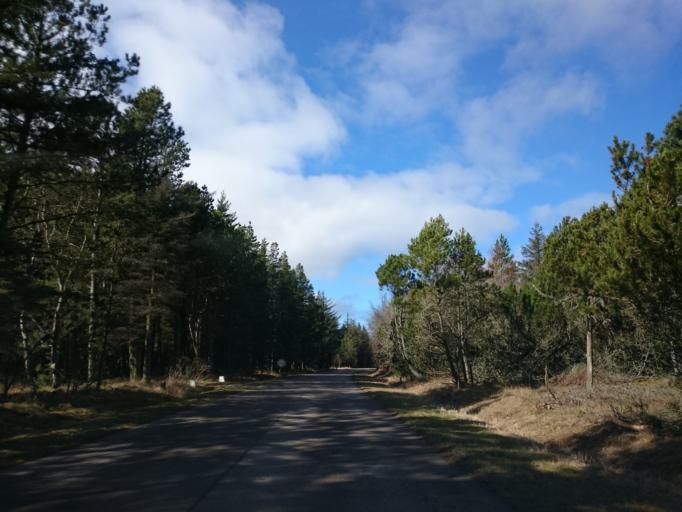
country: DK
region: North Denmark
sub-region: Frederikshavn Kommune
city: Skagen
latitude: 57.6542
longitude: 10.4232
